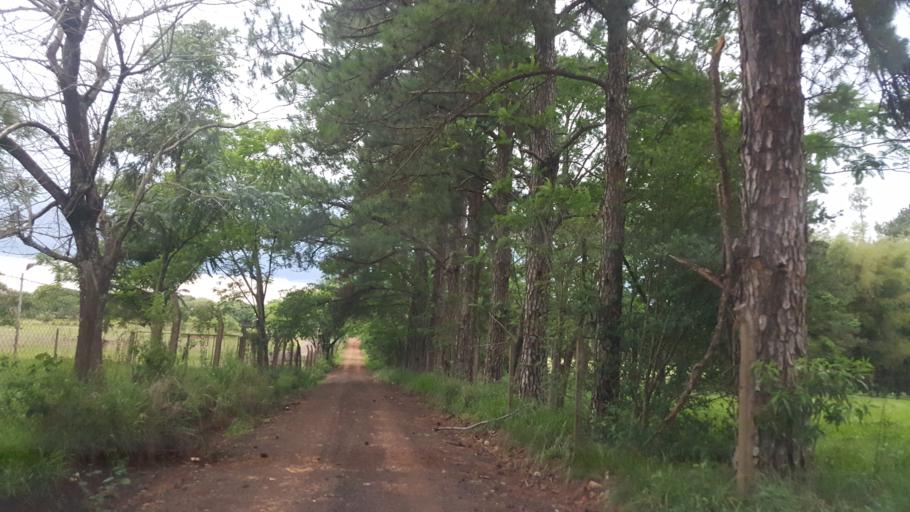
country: AR
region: Misiones
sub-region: Departamento de Capital
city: Posadas
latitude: -27.3996
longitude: -55.9733
